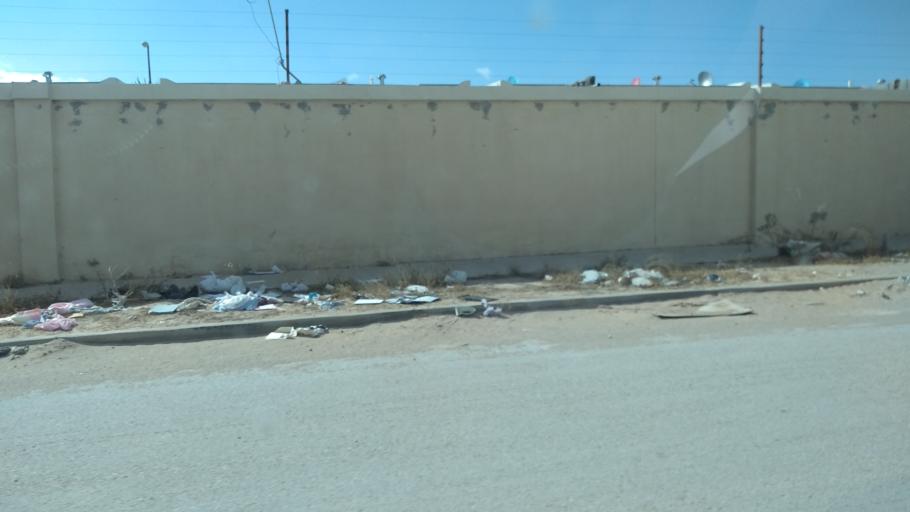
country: US
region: Texas
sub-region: El Paso County
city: San Elizario
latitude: 31.5789
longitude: -106.3300
